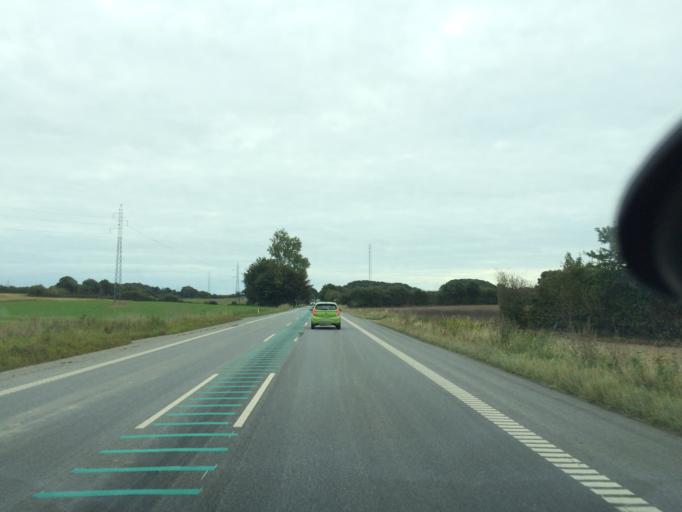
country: DK
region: South Denmark
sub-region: Aabenraa Kommune
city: Aabenraa
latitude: 54.9932
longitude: 9.4601
